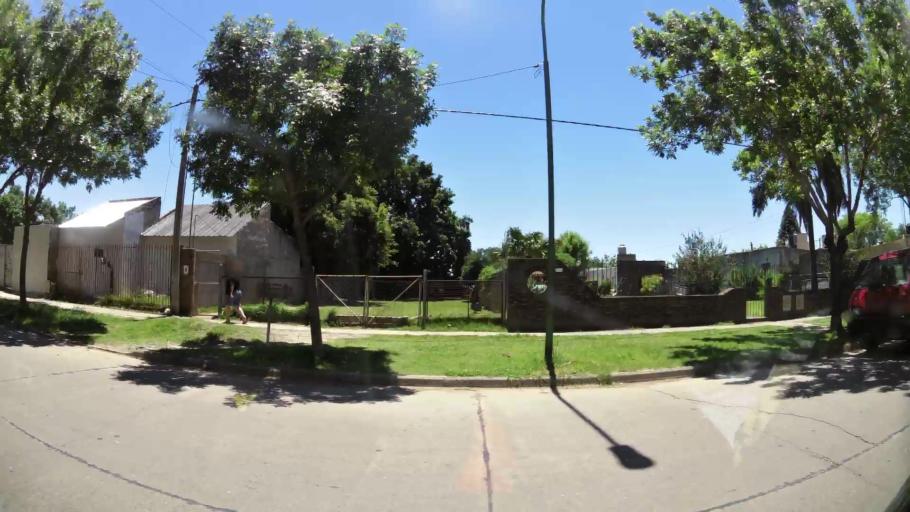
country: AR
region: Santa Fe
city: Rafaela
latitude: -31.2492
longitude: -61.4611
